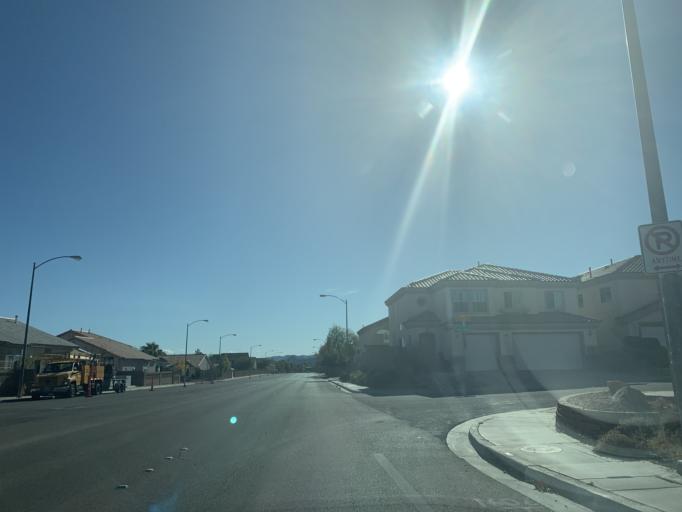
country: US
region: Nevada
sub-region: Clark County
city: Summerlin South
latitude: 36.1252
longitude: -115.3062
